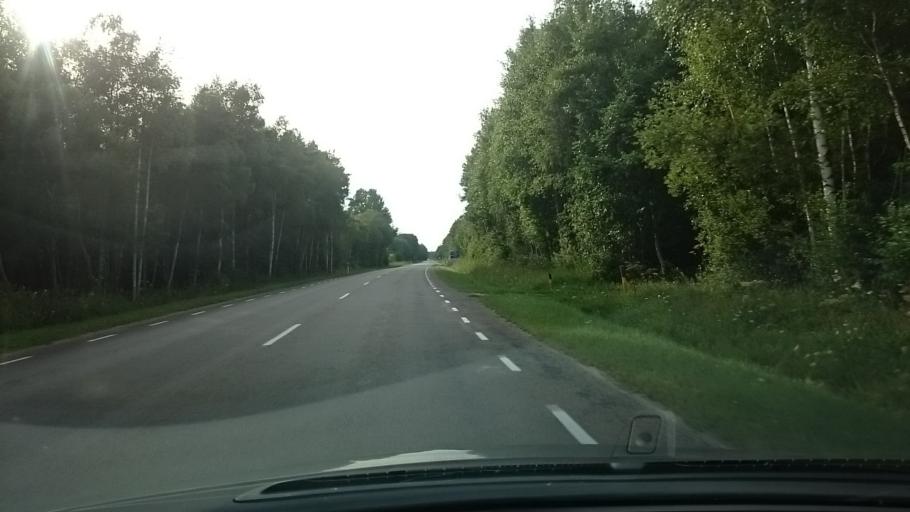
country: EE
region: Saare
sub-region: Kuressaare linn
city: Kuressaare
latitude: 58.2897
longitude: 22.3879
